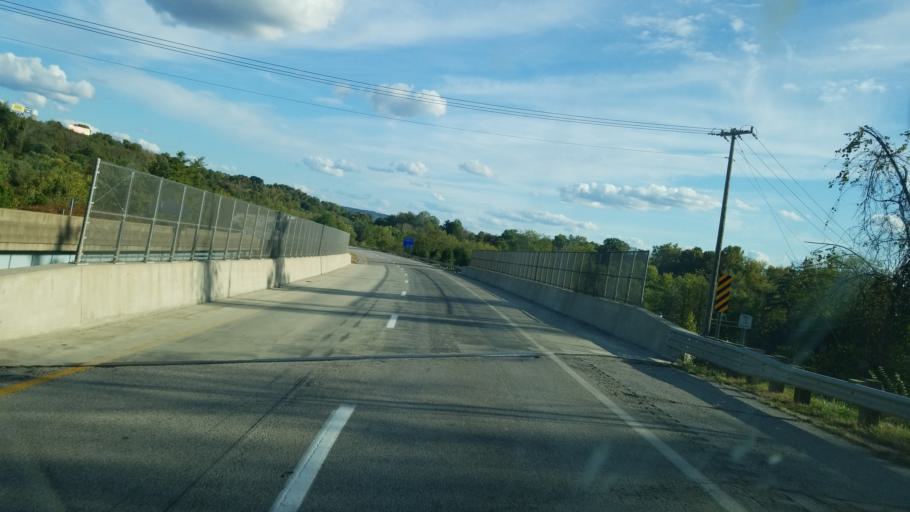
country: US
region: Ohio
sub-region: Washington County
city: Marietta
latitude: 39.4225
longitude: -81.4269
